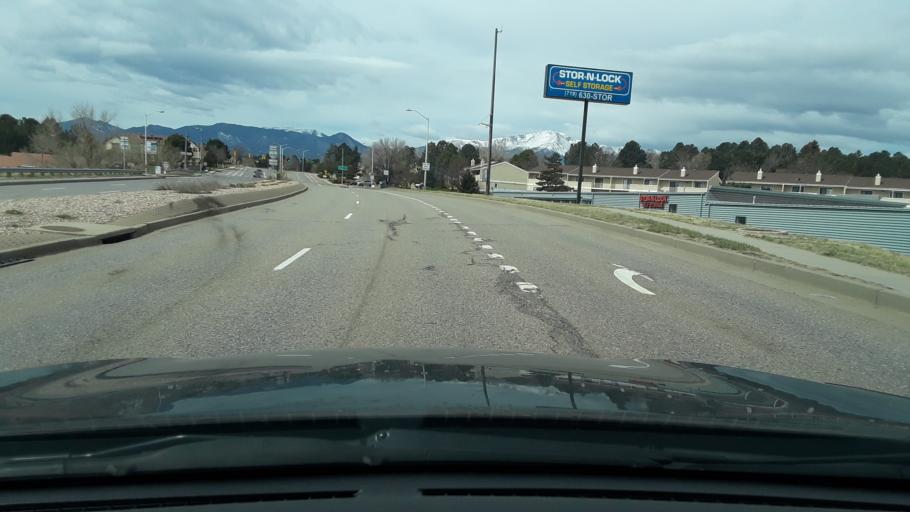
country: US
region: Colorado
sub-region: El Paso County
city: Air Force Academy
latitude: 38.9322
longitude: -104.8186
